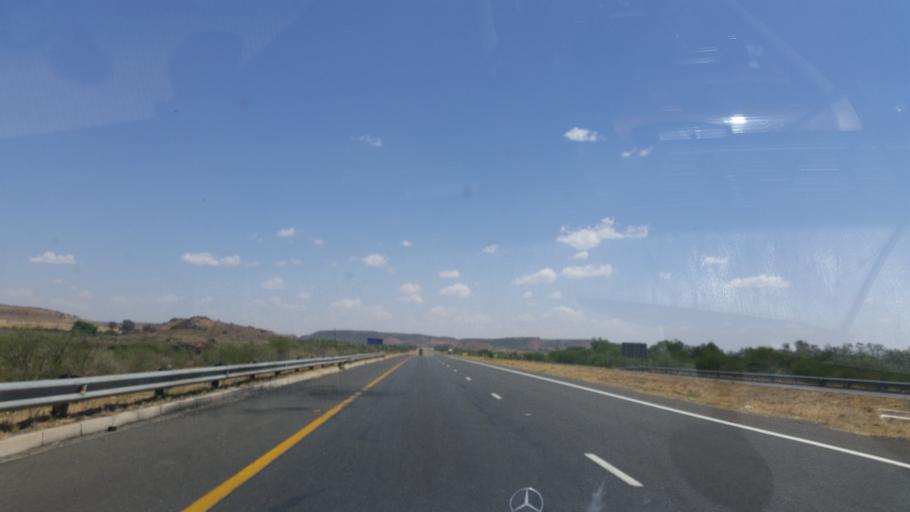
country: ZA
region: Orange Free State
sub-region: Mangaung Metropolitan Municipality
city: Bloemfontein
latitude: -28.9689
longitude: 26.3313
